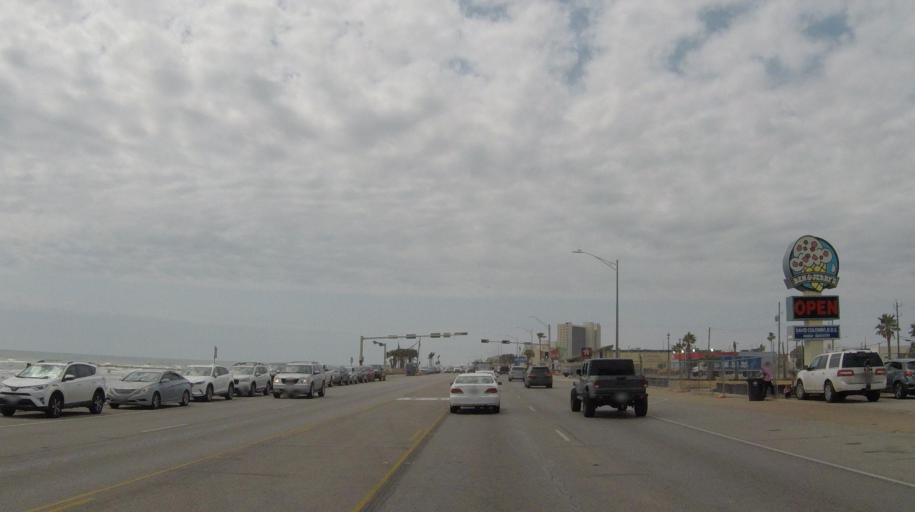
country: US
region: Texas
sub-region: Galveston County
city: Galveston
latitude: 29.2763
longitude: -94.8096
